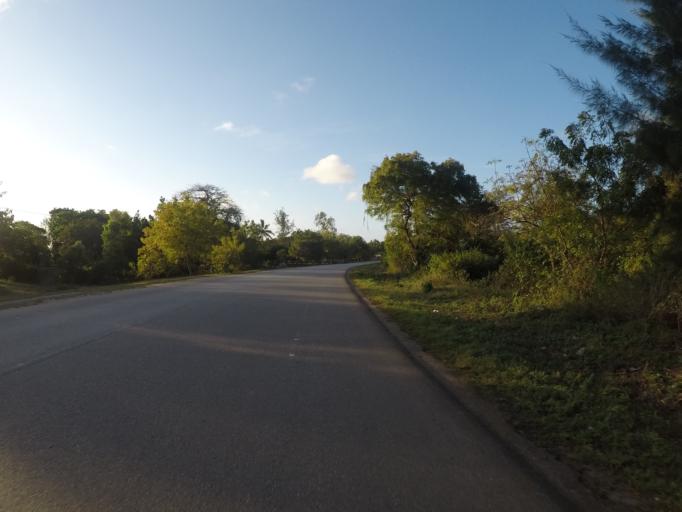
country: TZ
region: Zanzibar North
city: Kijini
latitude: -5.8225
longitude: 39.2913
